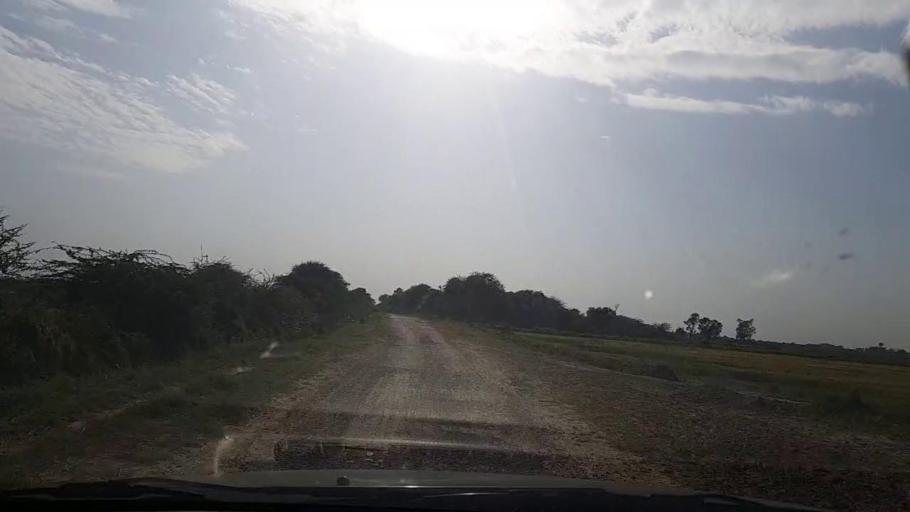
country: PK
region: Sindh
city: Mirpur Batoro
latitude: 24.5550
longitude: 68.1822
